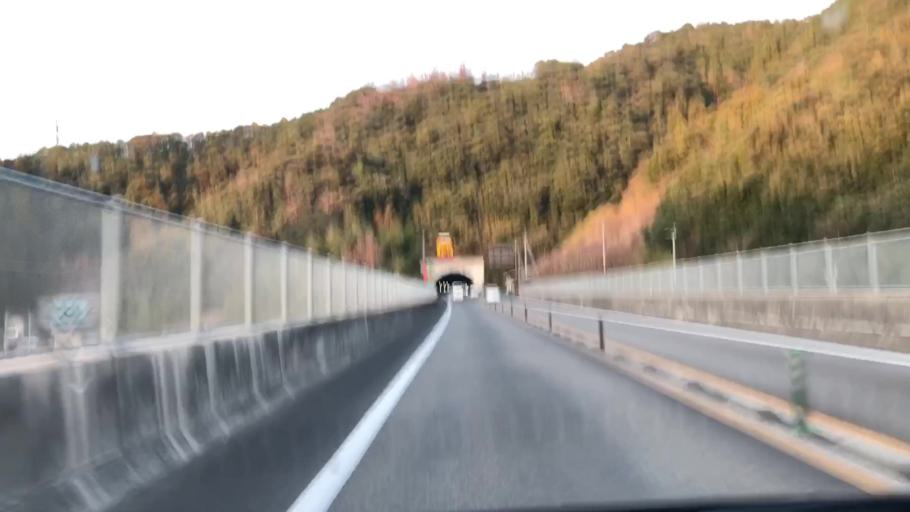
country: JP
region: Kumamoto
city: Minamata
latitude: 32.3021
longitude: 130.5107
